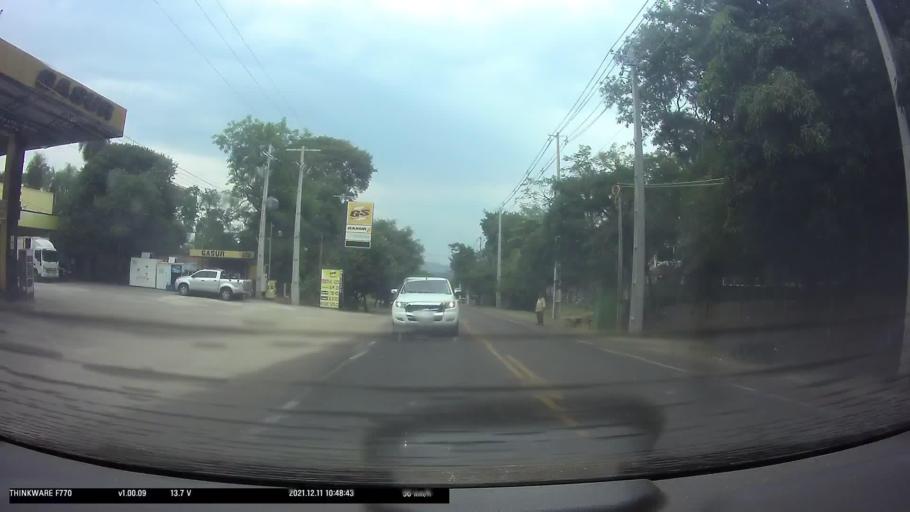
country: PY
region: Cordillera
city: San Bernardino
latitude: -25.2982
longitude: -57.2855
